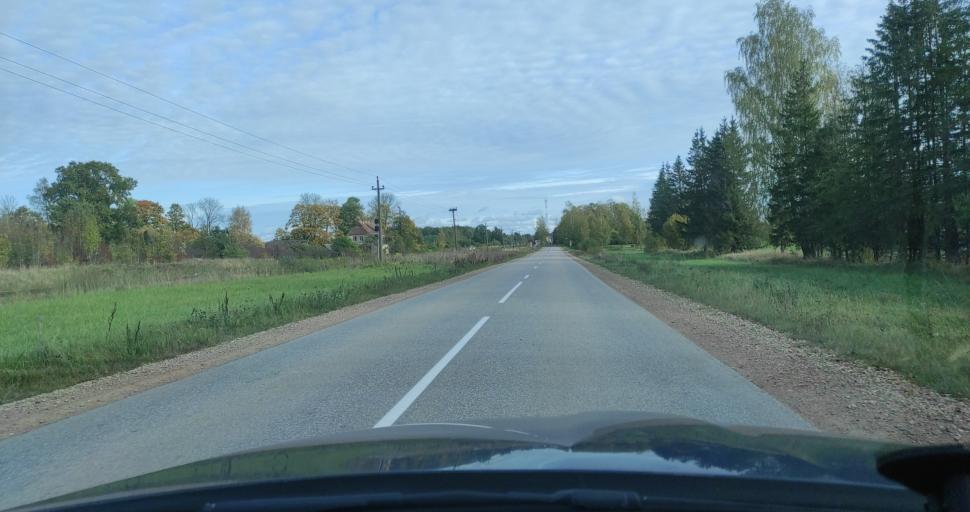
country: LV
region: Jaunpils
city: Jaunpils
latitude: 56.6898
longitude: 22.9712
